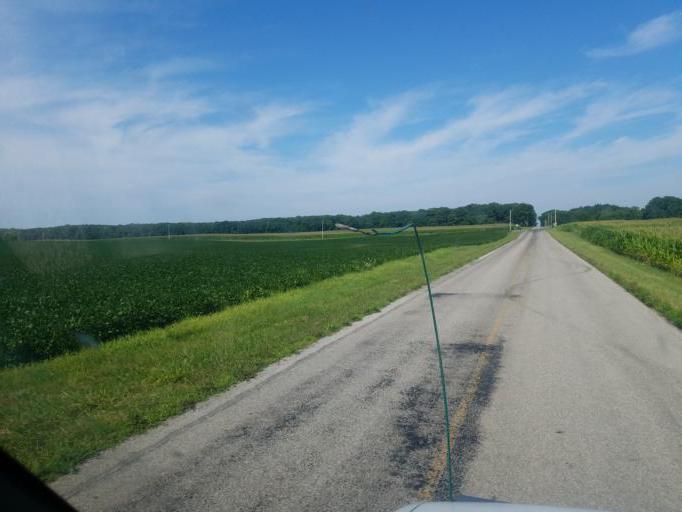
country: US
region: Ohio
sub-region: Hardin County
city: Kenton
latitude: 40.5552
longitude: -83.6384
